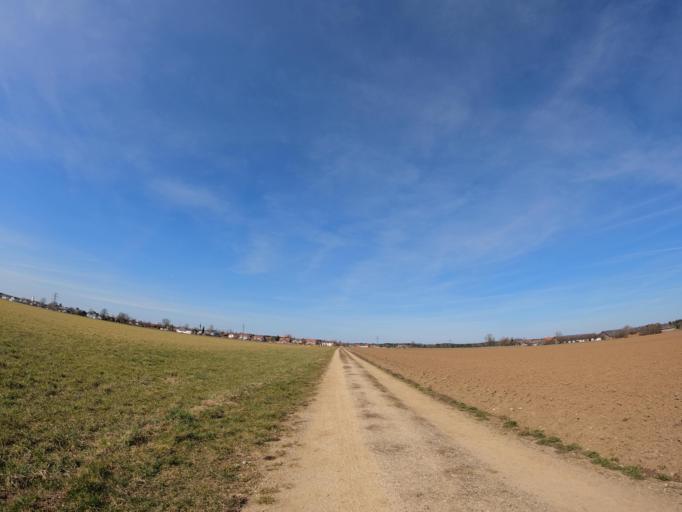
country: DE
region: Bavaria
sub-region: Upper Bavaria
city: Brunnthal
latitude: 48.0010
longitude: 11.6905
